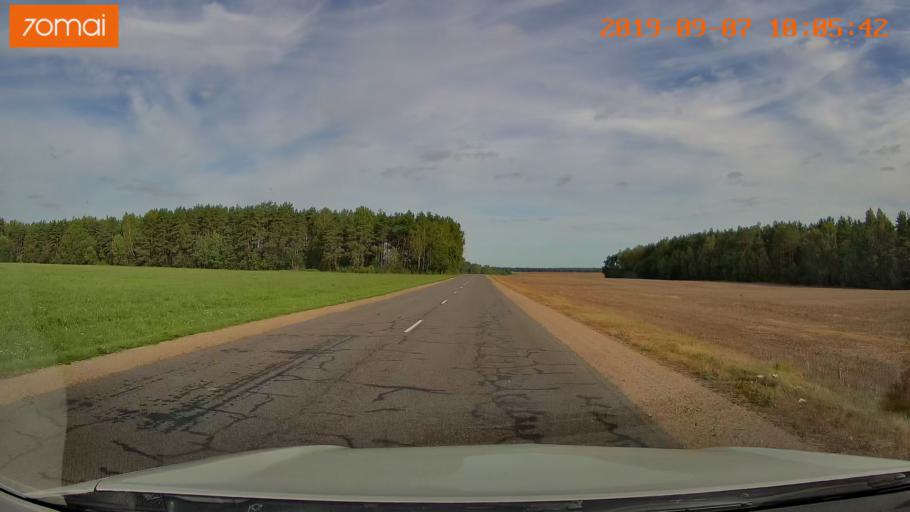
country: BY
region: Grodnenskaya
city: Voranava
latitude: 54.0511
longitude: 25.4061
